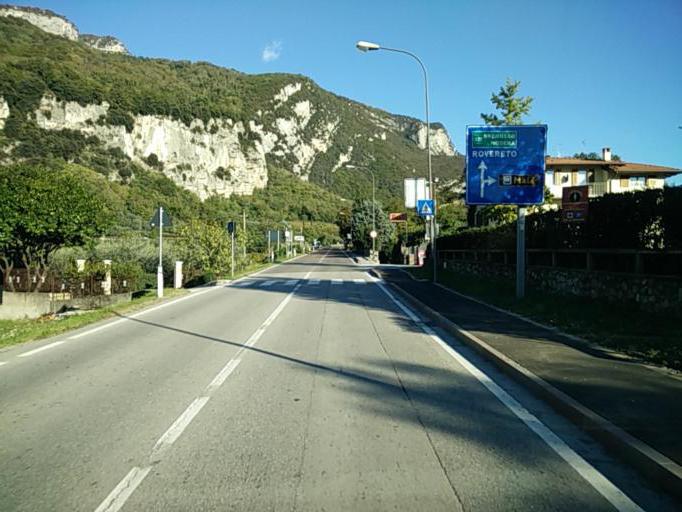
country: IT
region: Trentino-Alto Adige
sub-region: Provincia di Trento
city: Nago-Torbole
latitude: 45.8780
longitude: 10.8975
